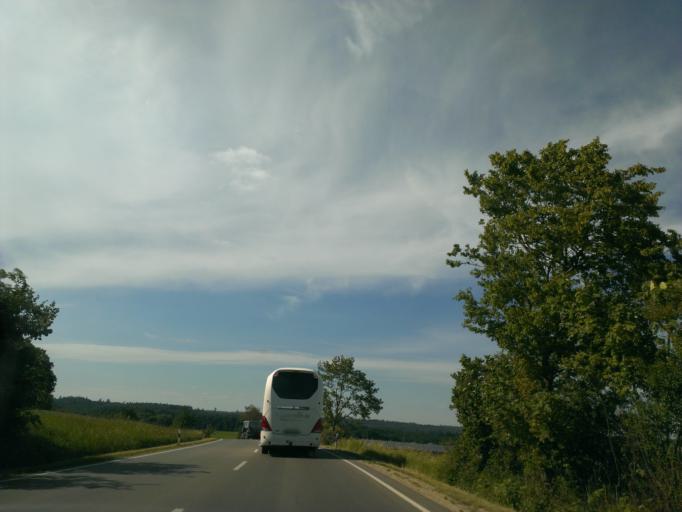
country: DE
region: Bavaria
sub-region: Swabia
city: Fremdingen
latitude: 48.9499
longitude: 10.4580
